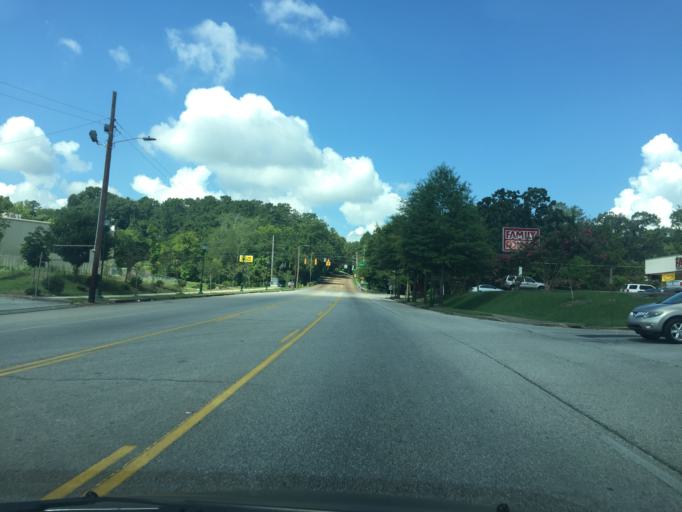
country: US
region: Tennessee
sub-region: Hamilton County
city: East Chattanooga
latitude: 35.0482
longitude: -85.2416
